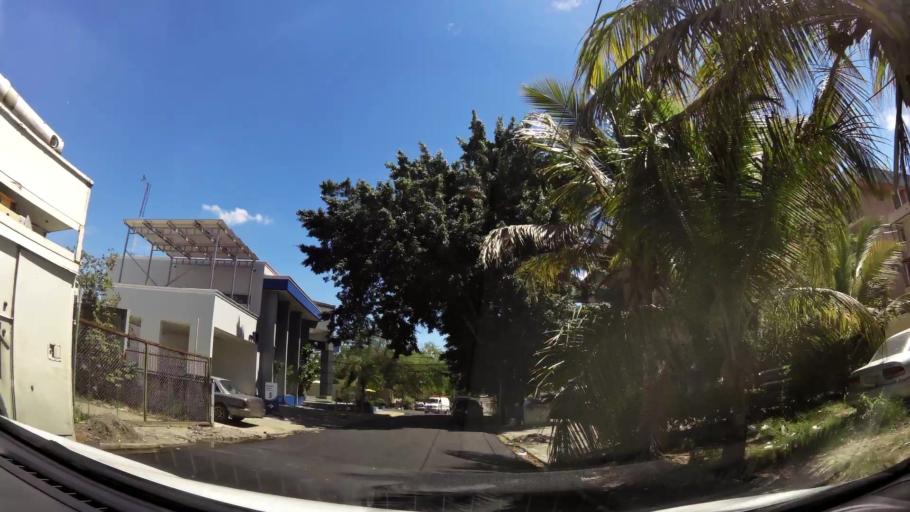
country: DO
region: Santiago
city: Santiago de los Caballeros
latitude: 19.4421
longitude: -70.7002
